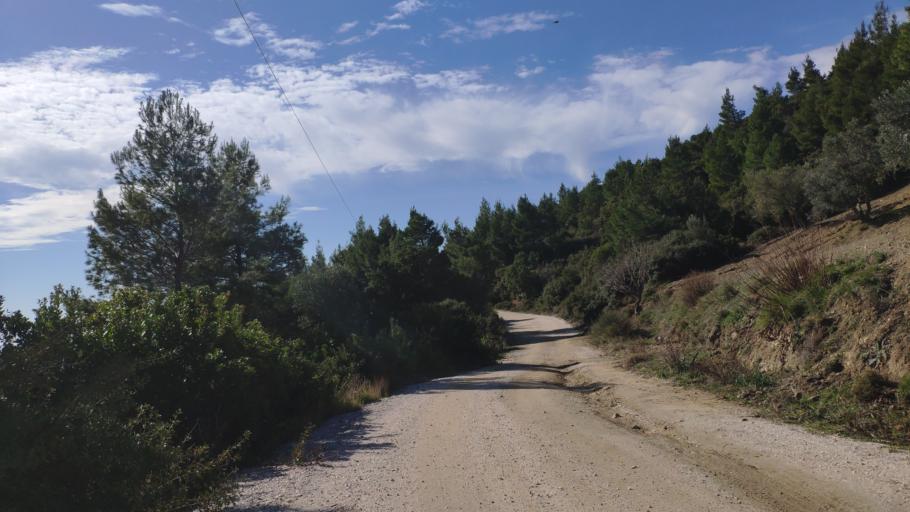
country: GR
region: Attica
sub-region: Nomarchia Anatolikis Attikis
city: Varybobi
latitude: 38.1503
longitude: 23.7746
